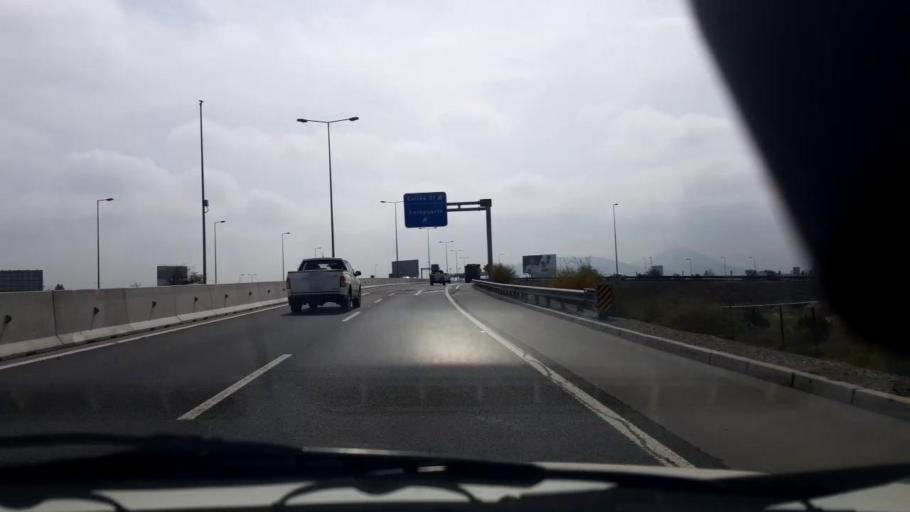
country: CL
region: Santiago Metropolitan
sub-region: Provincia de Santiago
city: Lo Prado
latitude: -33.4201
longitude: -70.7941
